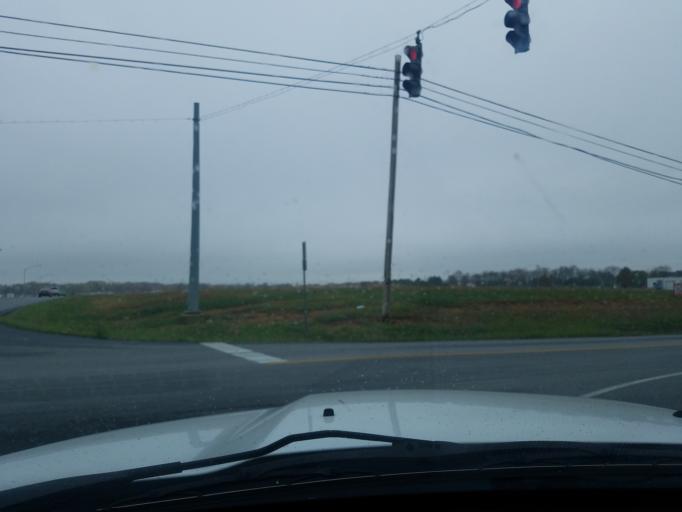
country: US
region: Kentucky
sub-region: Taylor County
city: Campbellsville
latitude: 37.3473
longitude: -85.3605
